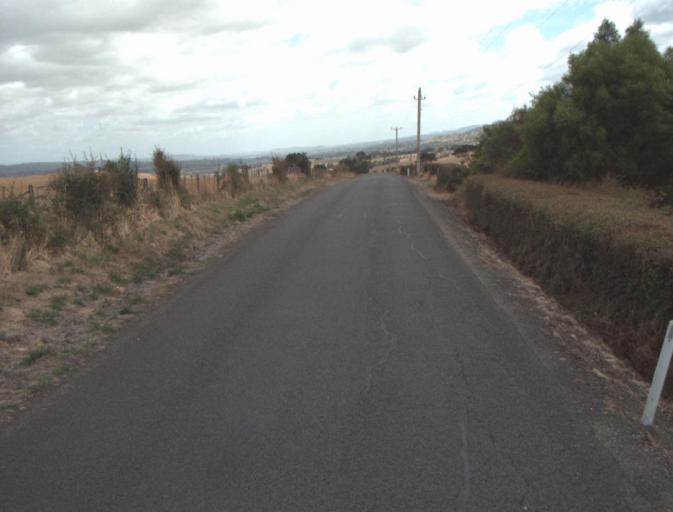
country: AU
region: Tasmania
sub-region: Northern Midlands
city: Evandale
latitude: -41.5129
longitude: 147.2527
